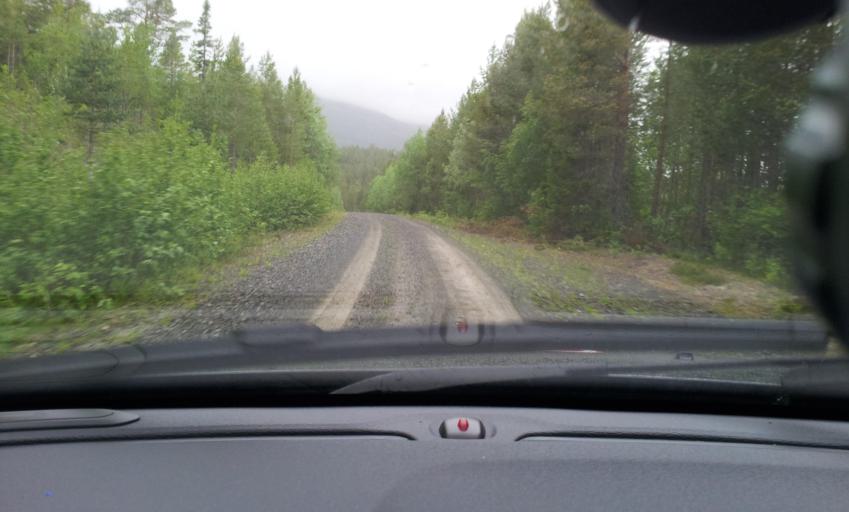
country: SE
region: Jaemtland
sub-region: Are Kommun
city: Jarpen
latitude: 63.1924
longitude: 13.4168
